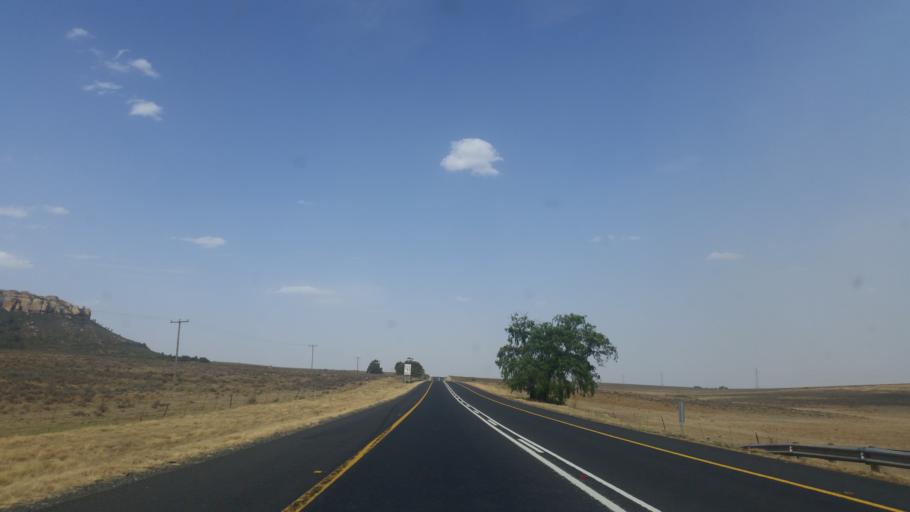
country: ZA
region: Orange Free State
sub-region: Thabo Mofutsanyana District Municipality
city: Bethlehem
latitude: -28.3017
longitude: 28.5535
